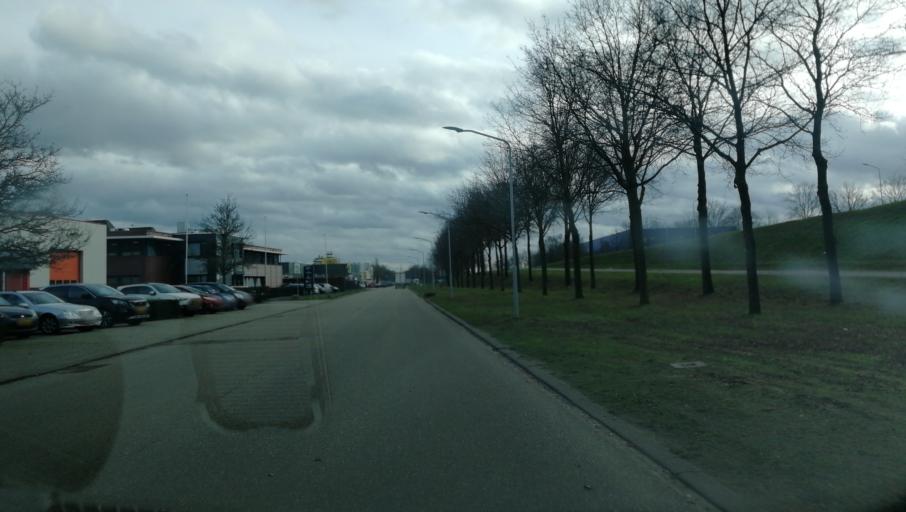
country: NL
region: Limburg
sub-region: Gemeente Venlo
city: Venlo
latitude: 51.3877
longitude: 6.1439
